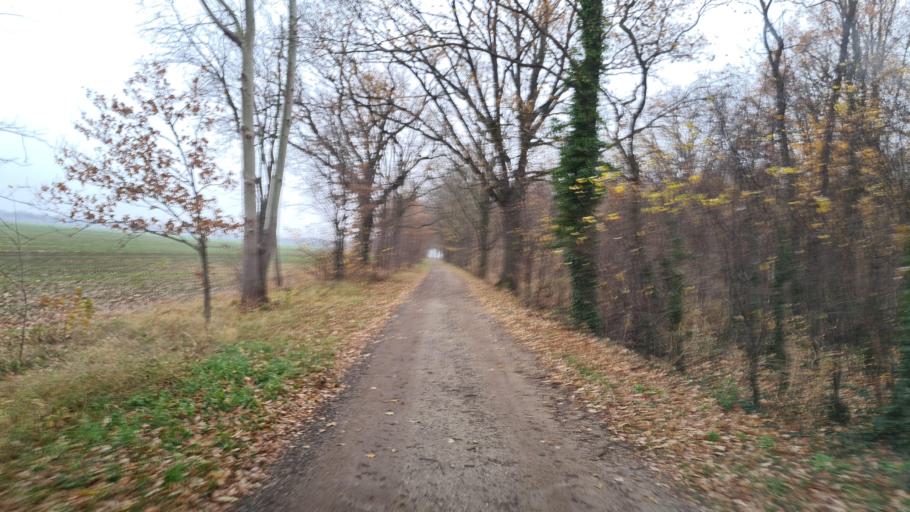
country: DE
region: Brandenburg
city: Lindenau
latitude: 51.4037
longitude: 13.7085
